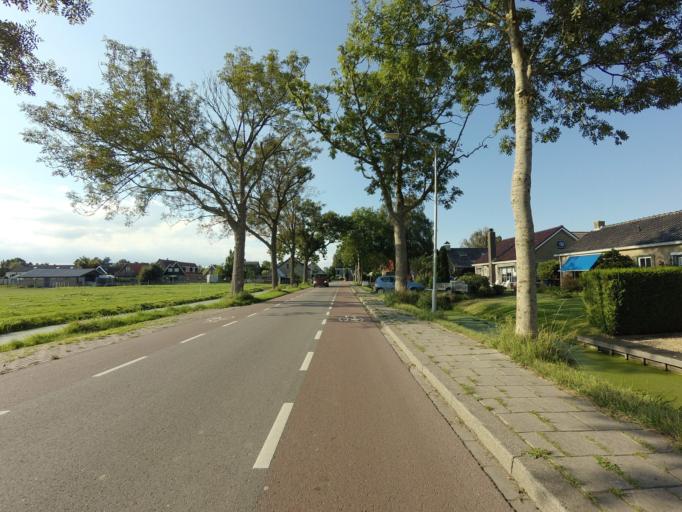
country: NL
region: North Holland
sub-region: Gemeente Hoorn
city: Hoorn
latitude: 52.6757
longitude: 5.1361
